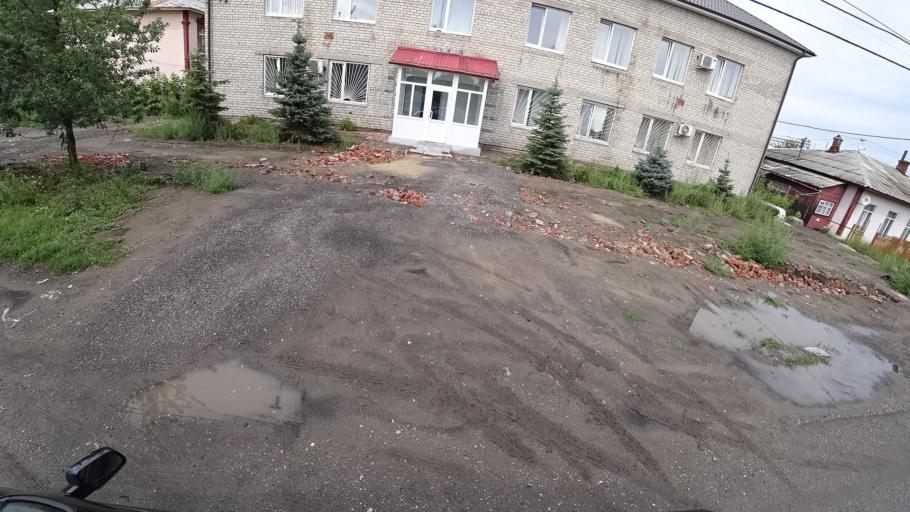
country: RU
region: Sverdlovsk
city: Kamyshlov
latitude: 56.8476
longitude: 62.7146
